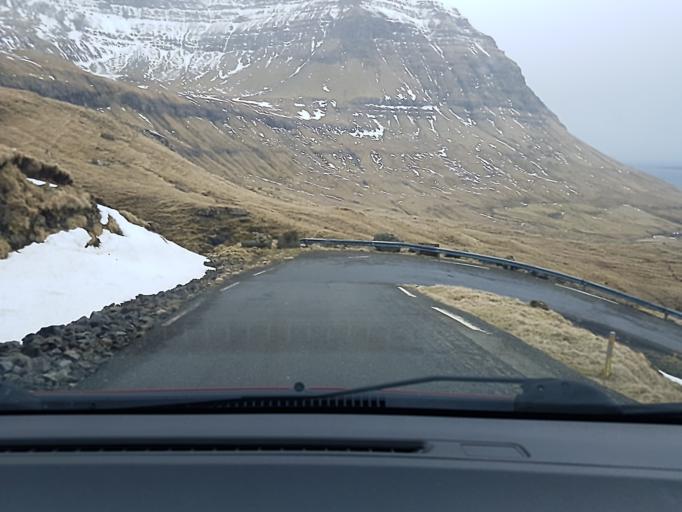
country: FO
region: Streymoy
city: Kollafjordhur
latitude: 62.0469
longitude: -6.9220
